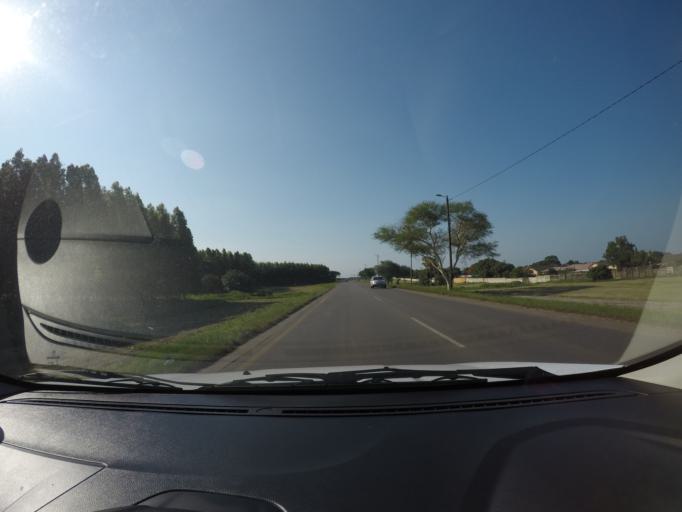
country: ZA
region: KwaZulu-Natal
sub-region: uThungulu District Municipality
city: Richards Bay
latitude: -28.7184
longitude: 32.0320
